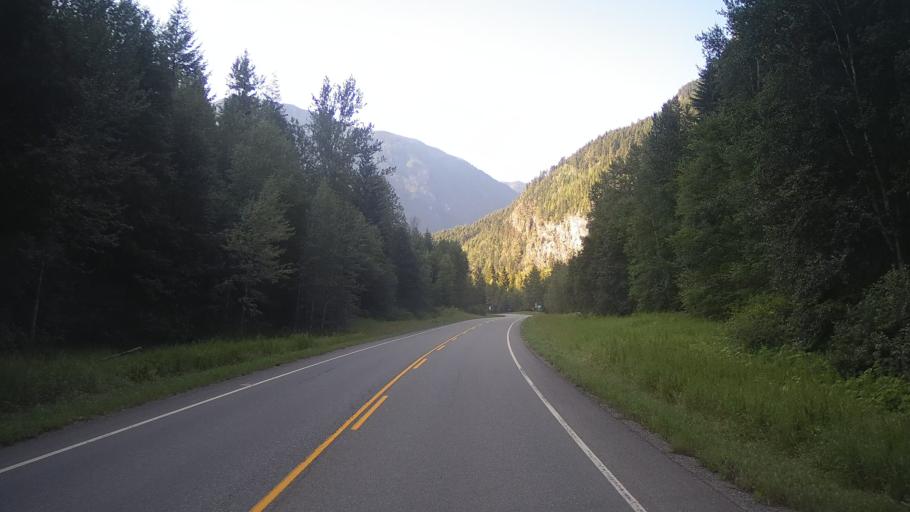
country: CA
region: British Columbia
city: Lillooet
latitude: 50.5897
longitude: -122.0938
